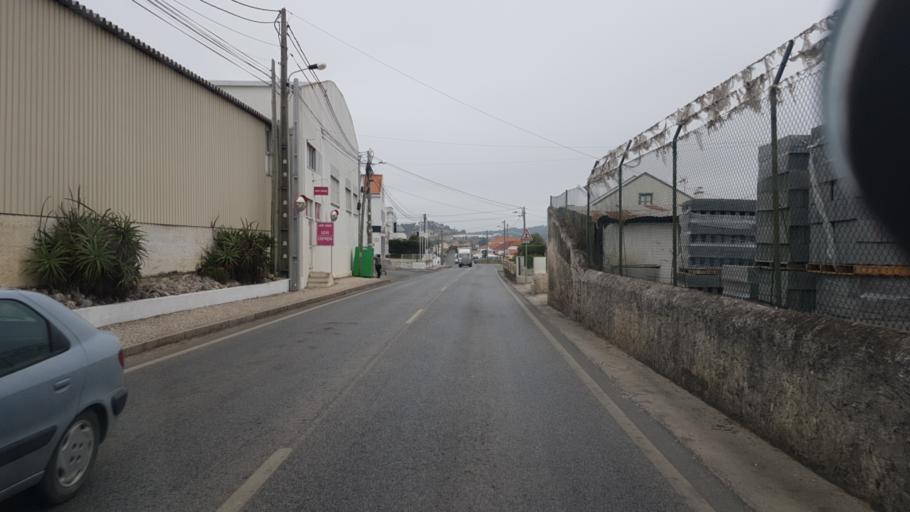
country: PT
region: Lisbon
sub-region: Torres Vedras
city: Torres Vedras
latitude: 39.0907
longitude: -9.3026
